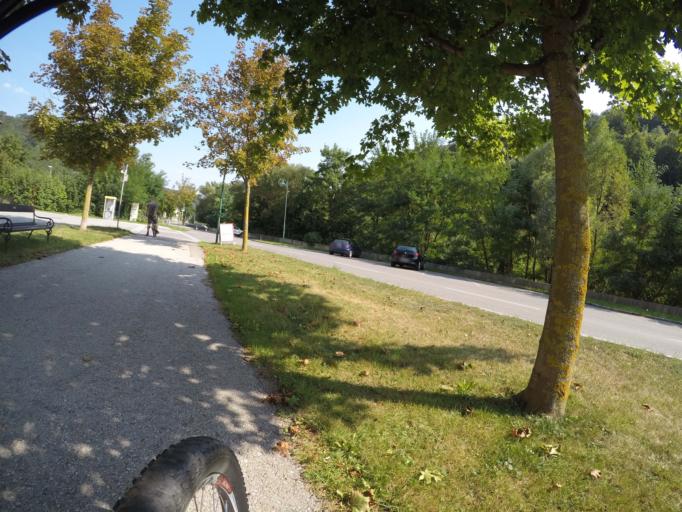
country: AT
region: Lower Austria
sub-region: Politischer Bezirk Baden
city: Weissenbach an der Triesting
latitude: 47.9835
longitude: 16.0460
